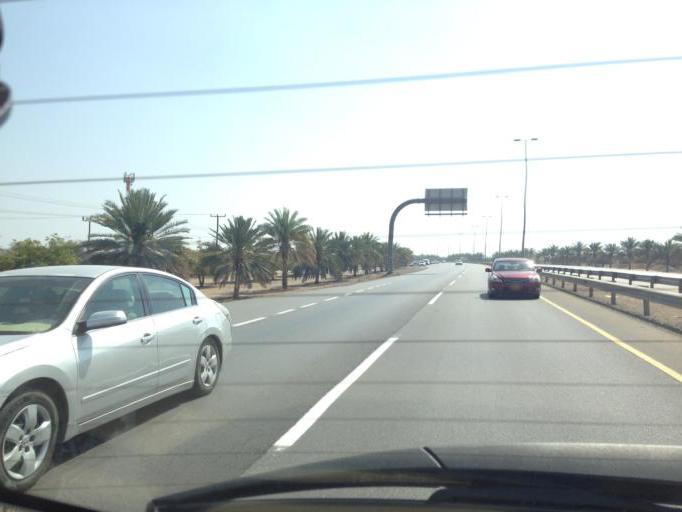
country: OM
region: Muhafazat Masqat
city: As Sib al Jadidah
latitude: 23.5899
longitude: 58.2200
